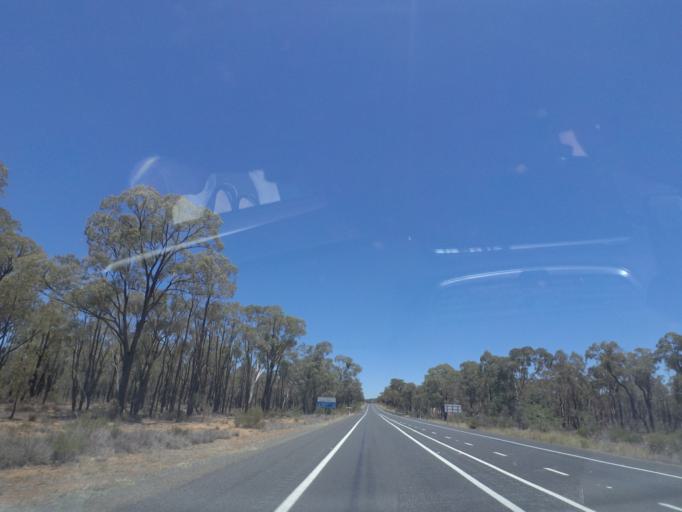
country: AU
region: New South Wales
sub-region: Warrumbungle Shire
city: Coonabarabran
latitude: -30.8800
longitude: 149.4467
